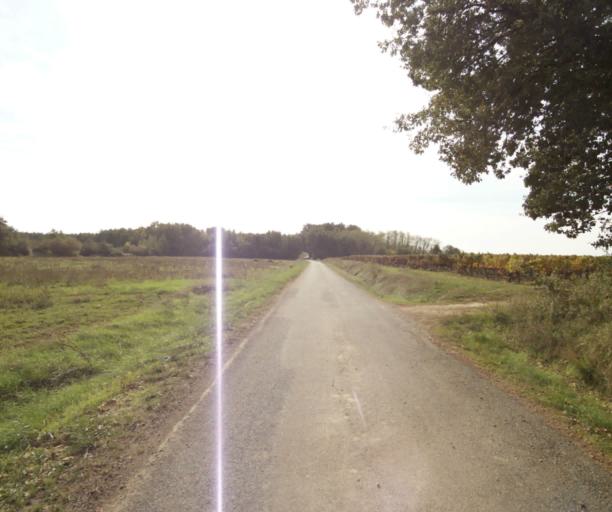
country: FR
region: Midi-Pyrenees
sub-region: Departement du Tarn-et-Garonne
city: Orgueil
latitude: 43.8878
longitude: 1.4028
